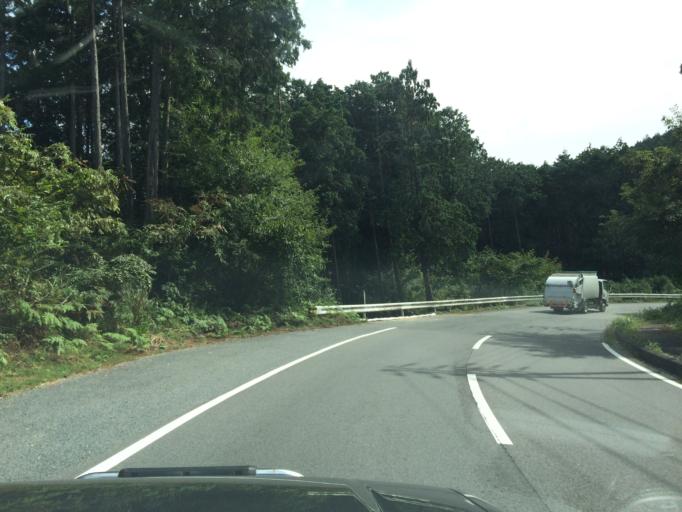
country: JP
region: Mie
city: Nabari
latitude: 34.6824
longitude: 136.0020
